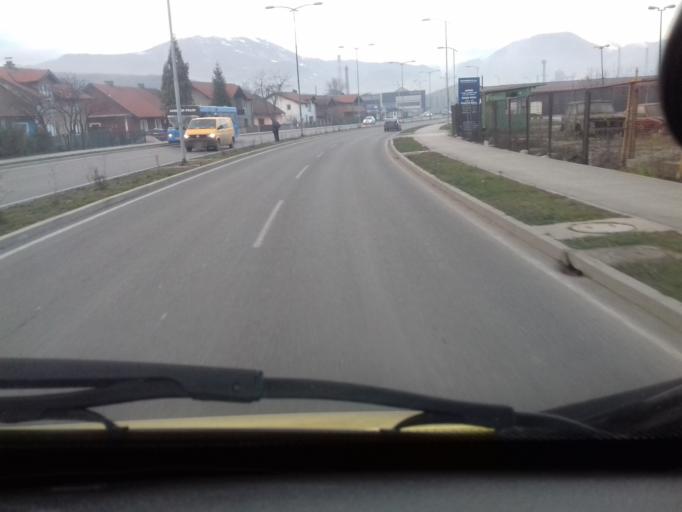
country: BA
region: Federation of Bosnia and Herzegovina
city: Zenica
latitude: 44.2054
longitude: 17.9026
